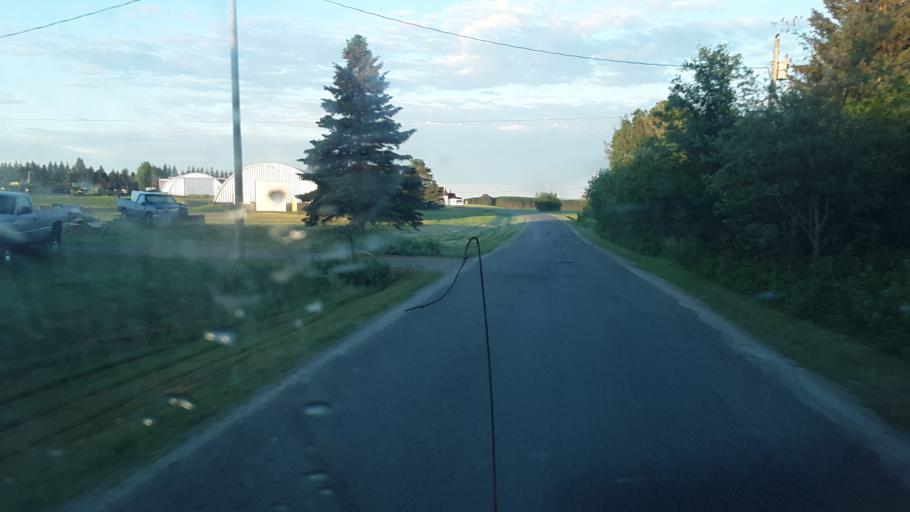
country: US
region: Maine
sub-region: Aroostook County
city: Caribou
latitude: 46.7783
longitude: -68.1011
